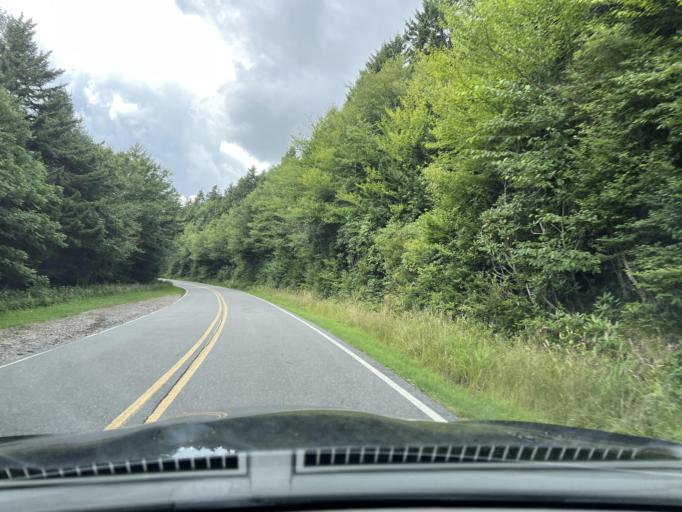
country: US
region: North Carolina
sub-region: Buncombe County
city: Black Mountain
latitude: 35.7401
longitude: -82.2790
